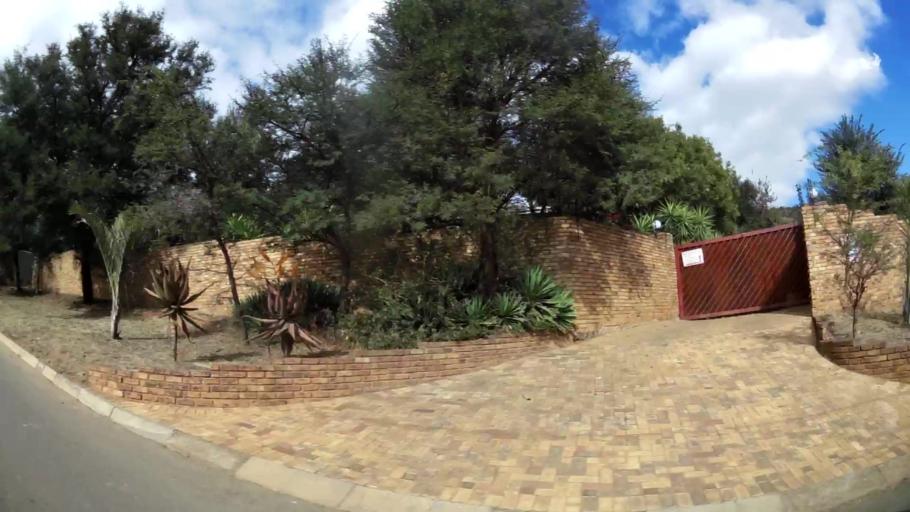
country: ZA
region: Gauteng
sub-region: West Rand District Municipality
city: Muldersdriseloop
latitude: -26.0929
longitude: 27.8523
